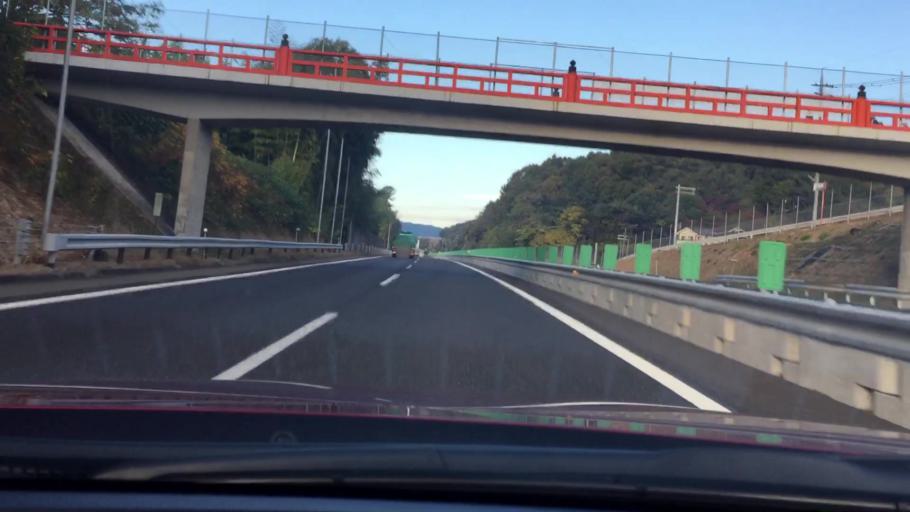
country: JP
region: Hyogo
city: Yamazakicho-nakabirose
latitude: 34.9899
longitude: 134.5916
